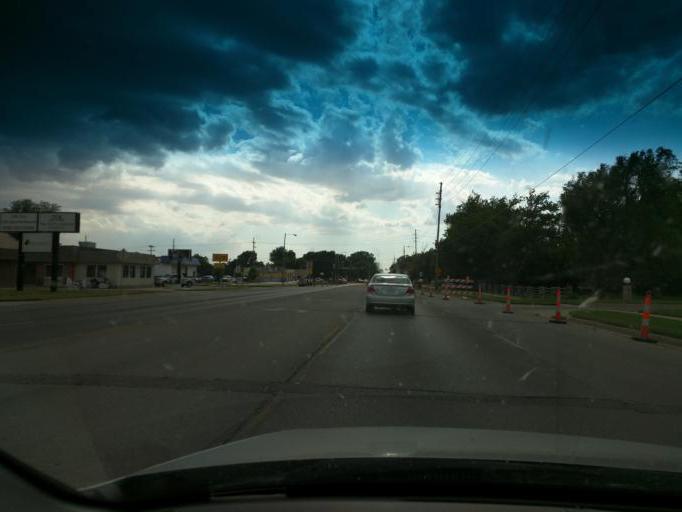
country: US
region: Kansas
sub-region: Reno County
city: Hutchinson
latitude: 38.0866
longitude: -97.9292
